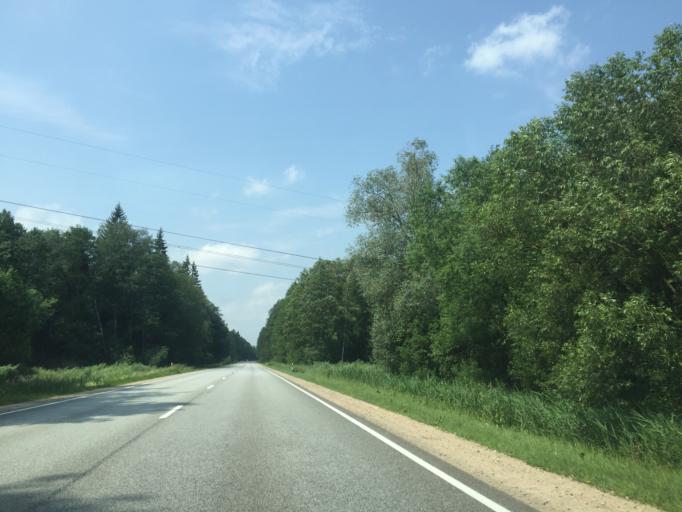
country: LV
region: Kekava
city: Balozi
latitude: 56.8207
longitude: 24.0940
